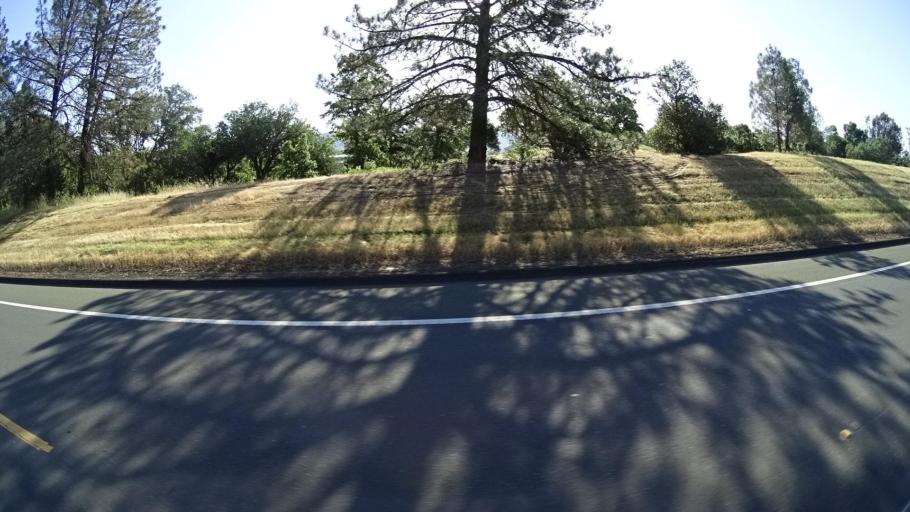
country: US
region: California
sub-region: Lake County
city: Upper Lake
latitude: 39.1334
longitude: -122.9089
